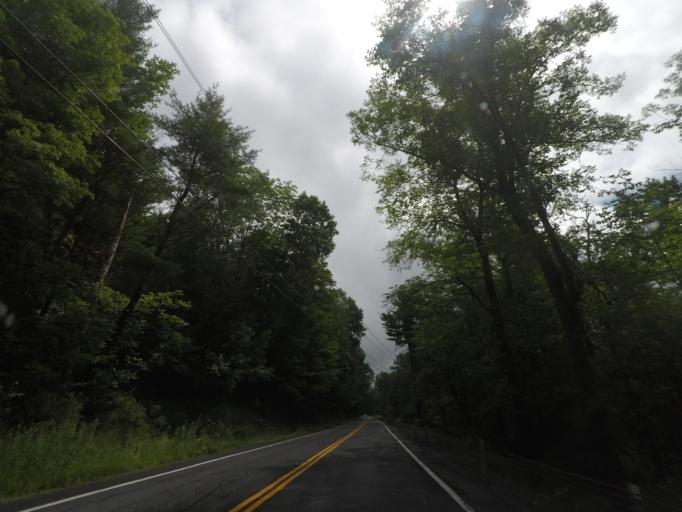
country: US
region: New York
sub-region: Rensselaer County
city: Averill Park
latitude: 42.5943
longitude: -73.5041
